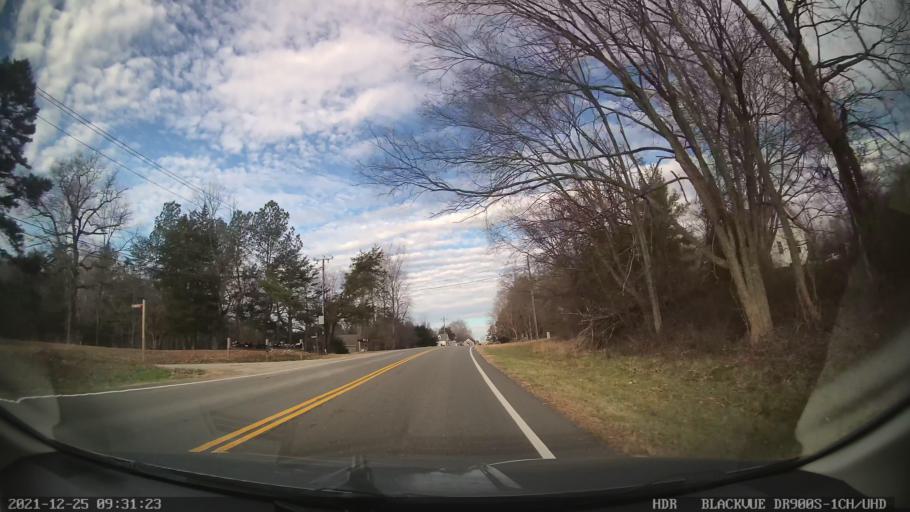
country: US
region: Virginia
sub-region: Goochland County
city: Goochland
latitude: 37.7148
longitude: -77.8208
